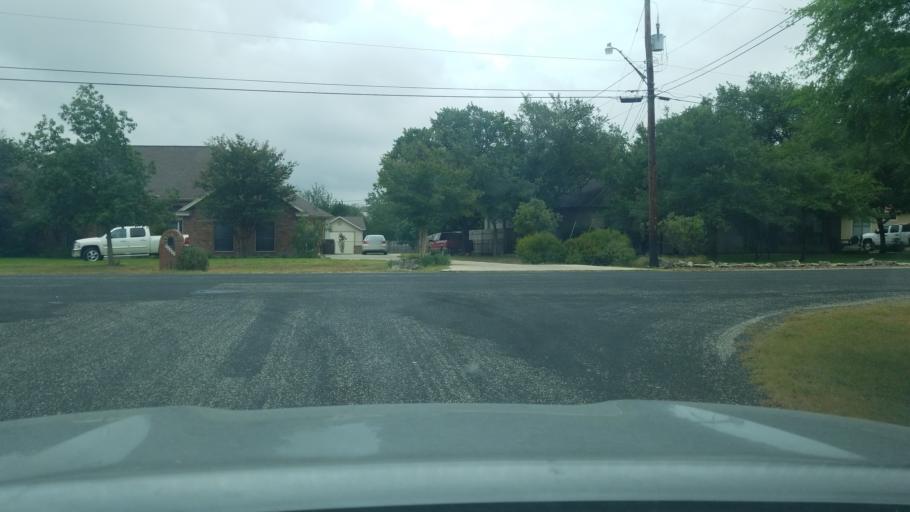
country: US
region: Texas
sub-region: Bexar County
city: Timberwood Park
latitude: 29.7039
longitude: -98.5098
